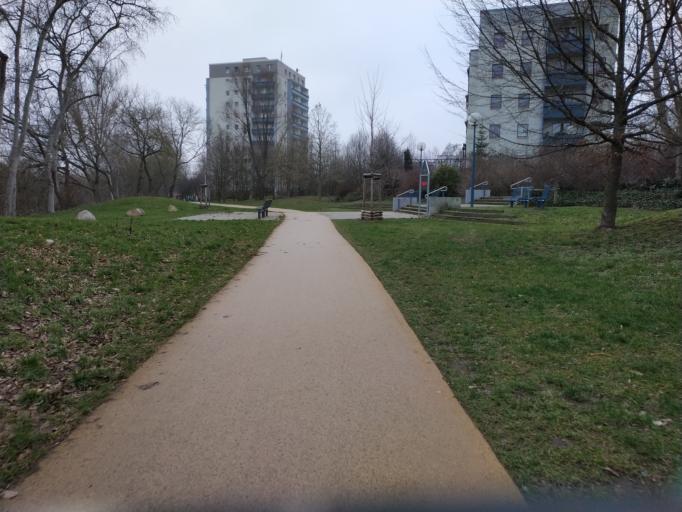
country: DE
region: Berlin
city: Marzahn
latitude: 52.5379
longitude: 13.5857
